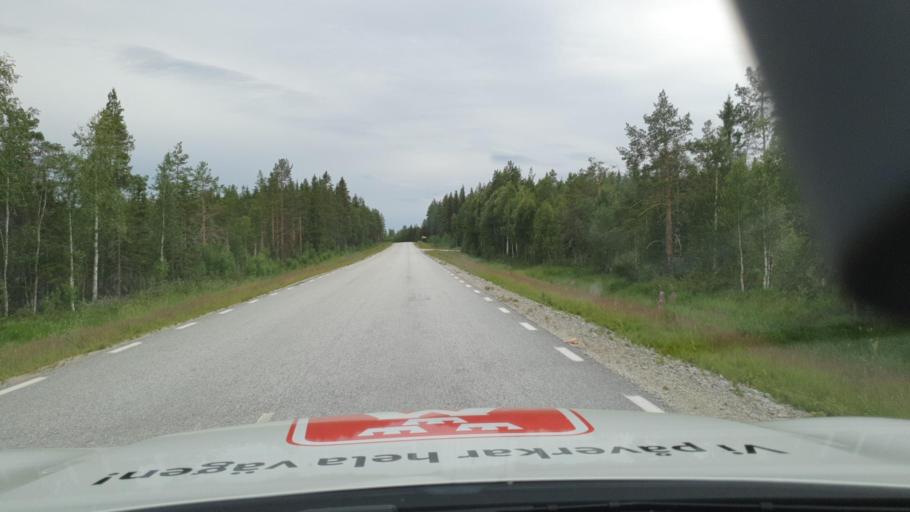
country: SE
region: Vaesterbotten
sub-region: Bjurholms Kommun
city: Bjurholm
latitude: 64.1568
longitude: 19.3611
